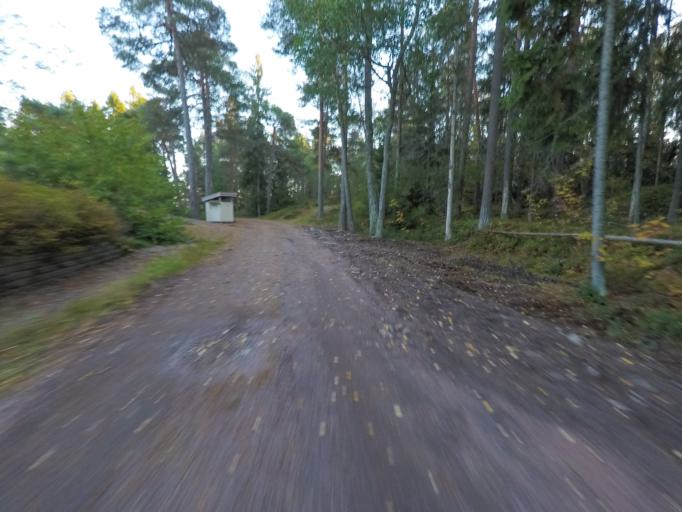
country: FI
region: Uusimaa
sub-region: Helsinki
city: Vantaa
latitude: 60.1597
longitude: 25.0746
